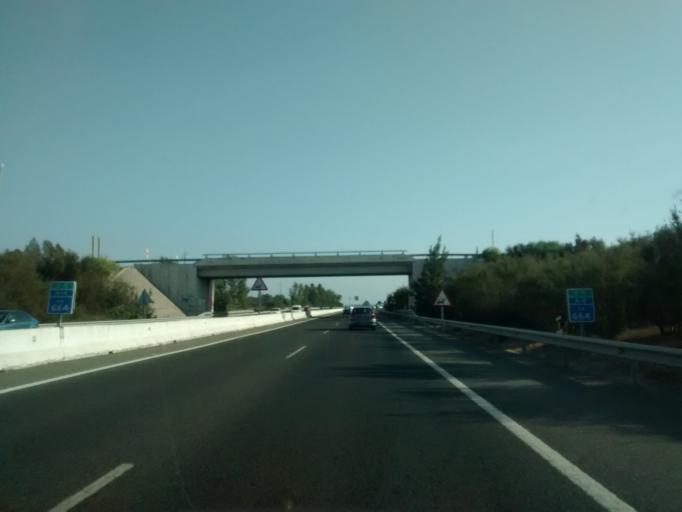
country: ES
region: Andalusia
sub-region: Provincia de Cadiz
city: Puerto Real
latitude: 36.4971
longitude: -6.1441
